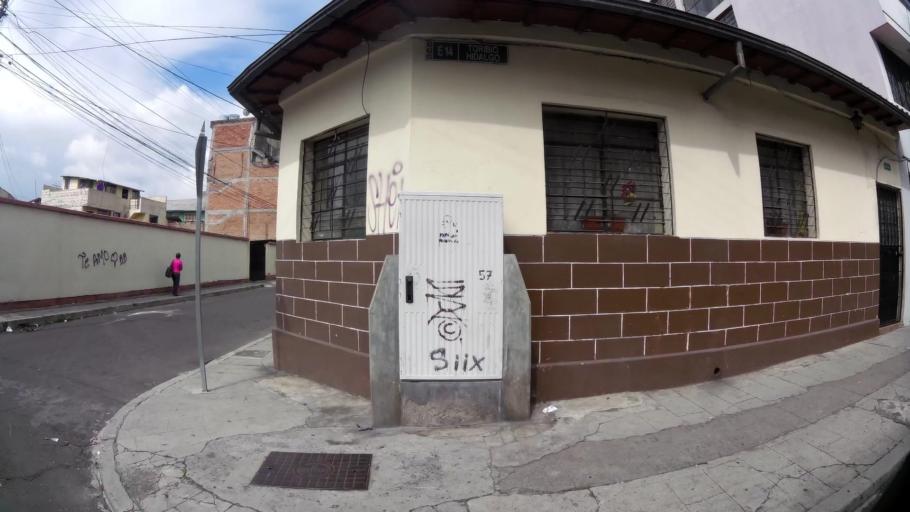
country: EC
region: Pichincha
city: Quito
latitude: -0.2177
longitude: -78.4885
